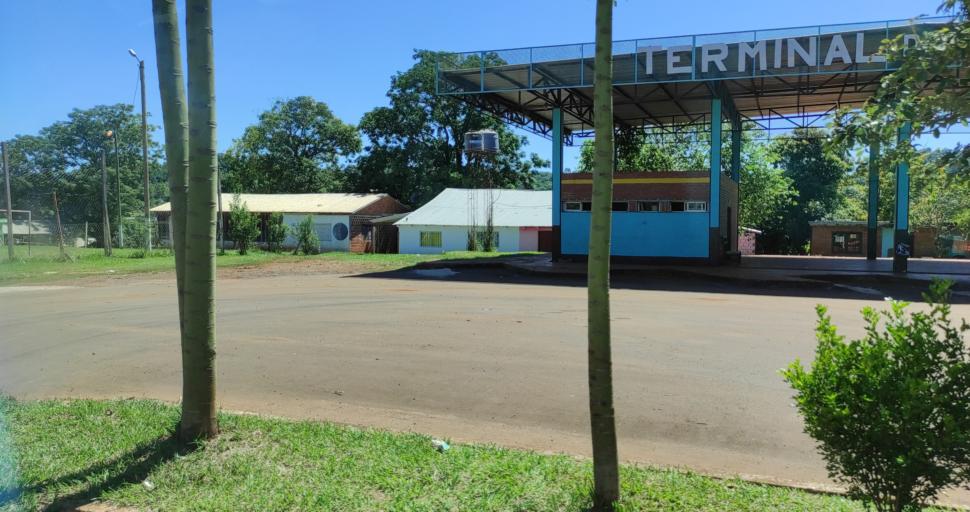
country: AR
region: Misiones
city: El Soberbio
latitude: -27.3007
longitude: -54.1940
